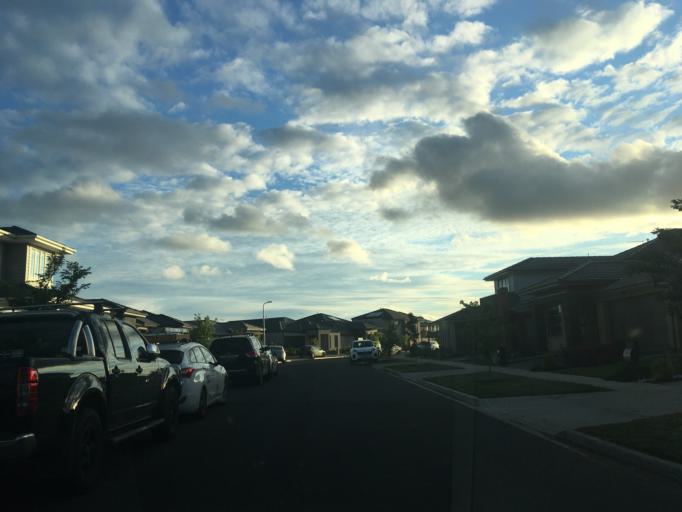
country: AU
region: Victoria
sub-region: Wyndham
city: Hoppers Crossing
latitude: -37.8876
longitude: 144.7124
